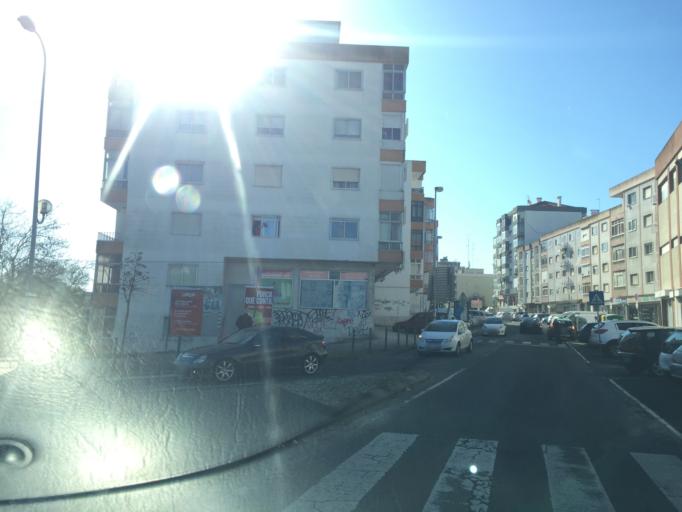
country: PT
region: Lisbon
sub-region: Sintra
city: Queluz
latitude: 38.7604
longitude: -9.2501
